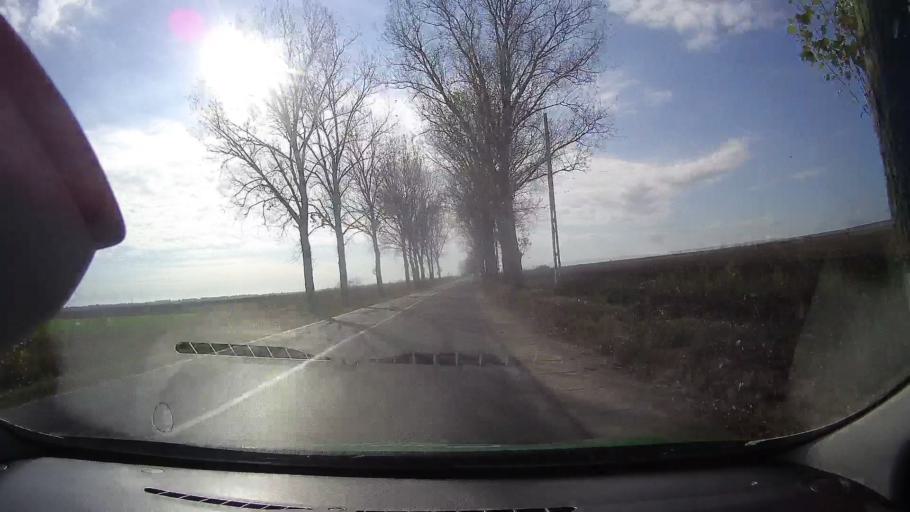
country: RO
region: Tulcea
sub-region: Comuna Valea Nucarilor
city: Agighiol
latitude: 44.9962
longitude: 28.8866
